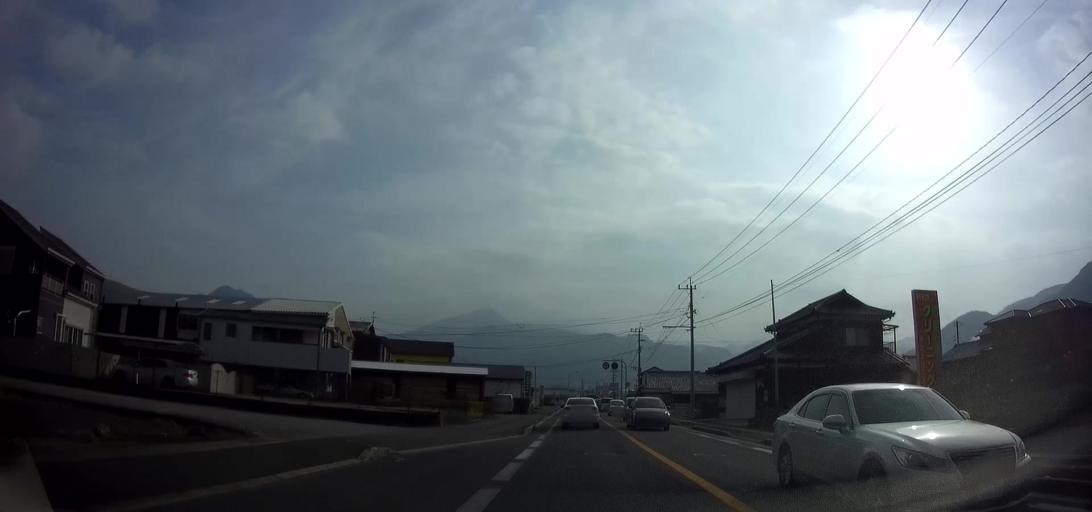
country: JP
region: Nagasaki
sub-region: Isahaya-shi
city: Isahaya
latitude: 32.7878
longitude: 130.1927
